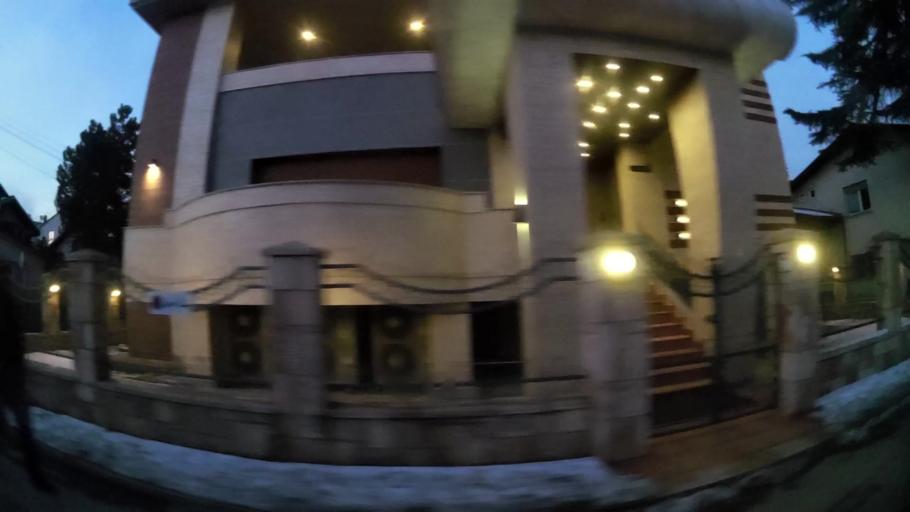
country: MK
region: Karpos
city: Skopje
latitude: 41.9979
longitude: 21.4070
